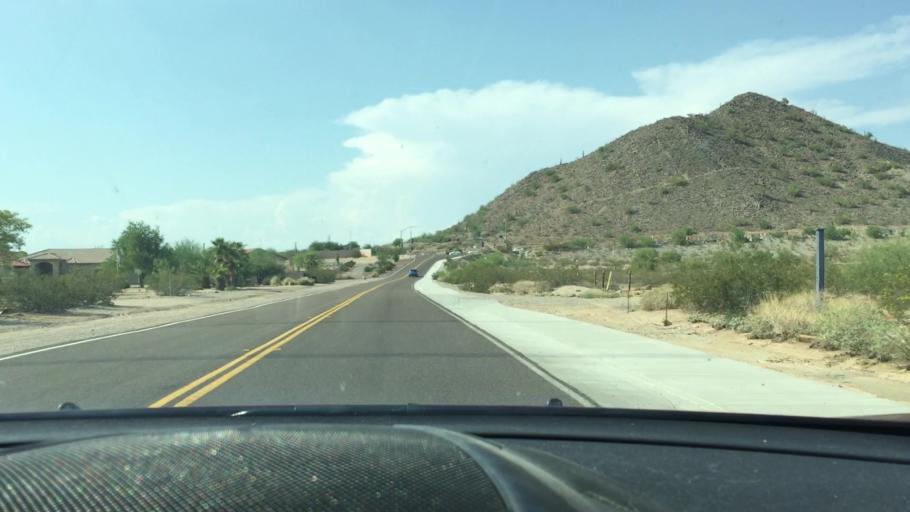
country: US
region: Arizona
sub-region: Maricopa County
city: Sun City West
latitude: 33.7074
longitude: -112.2549
